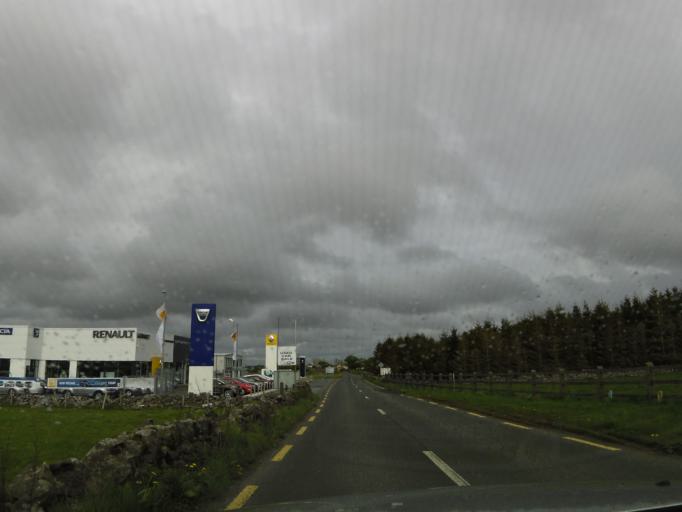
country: IE
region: Connaught
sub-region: Maigh Eo
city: Ballinrobe
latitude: 53.6275
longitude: -9.2136
